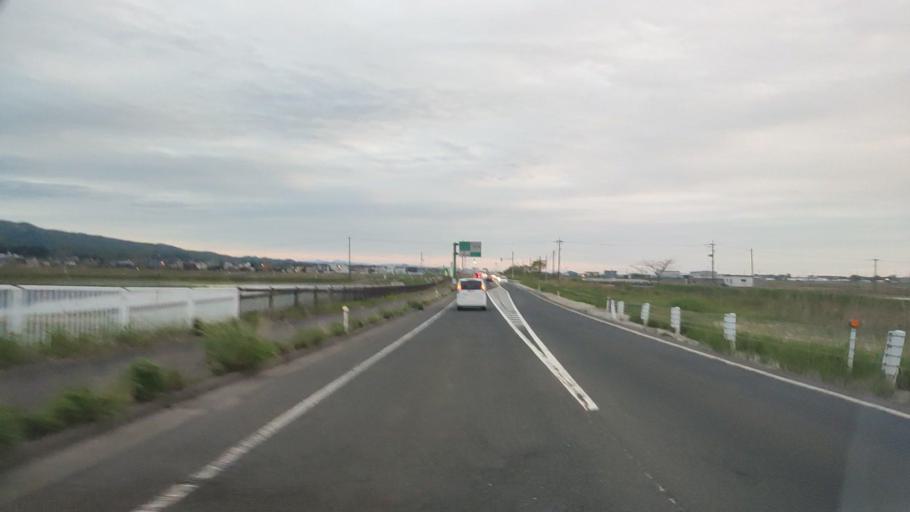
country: JP
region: Niigata
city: Niitsu-honcho
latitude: 37.7578
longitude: 139.0928
